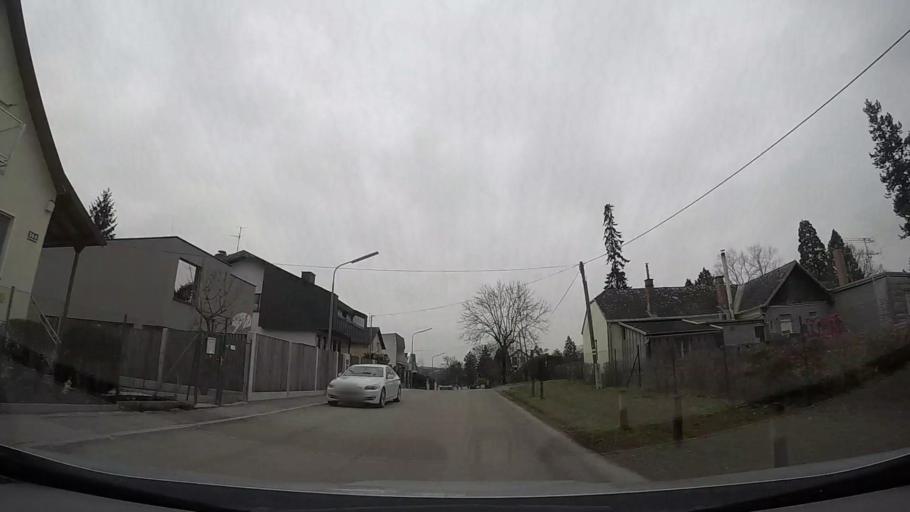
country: AT
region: Lower Austria
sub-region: Politischer Bezirk Wien-Umgebung
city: Purkersdorf
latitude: 48.2192
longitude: 16.2412
